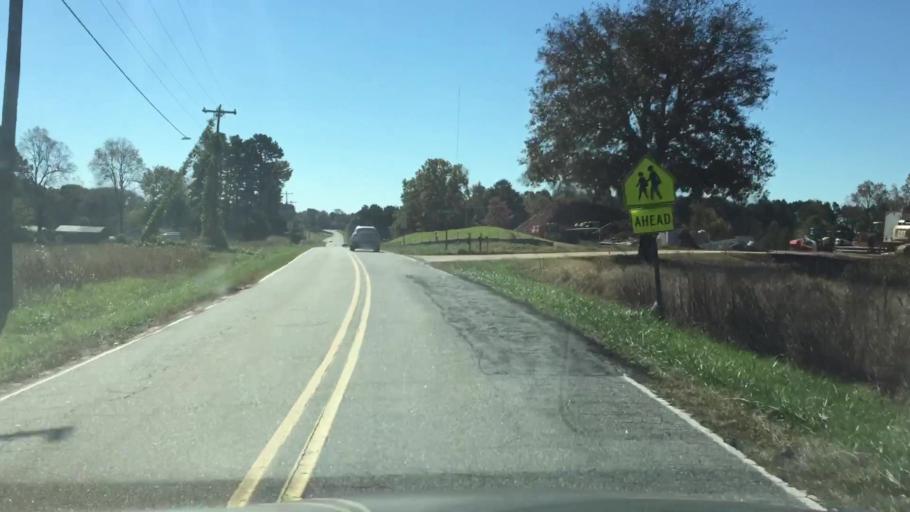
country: US
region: North Carolina
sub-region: Iredell County
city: Mooresville
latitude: 35.5592
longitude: -80.7906
